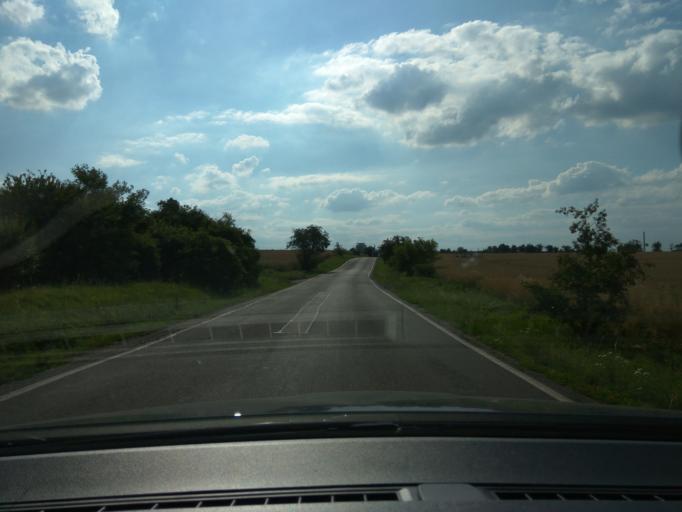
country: CZ
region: Praha
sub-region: Praha 19
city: Kbely
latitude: 50.1473
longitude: 14.5507
